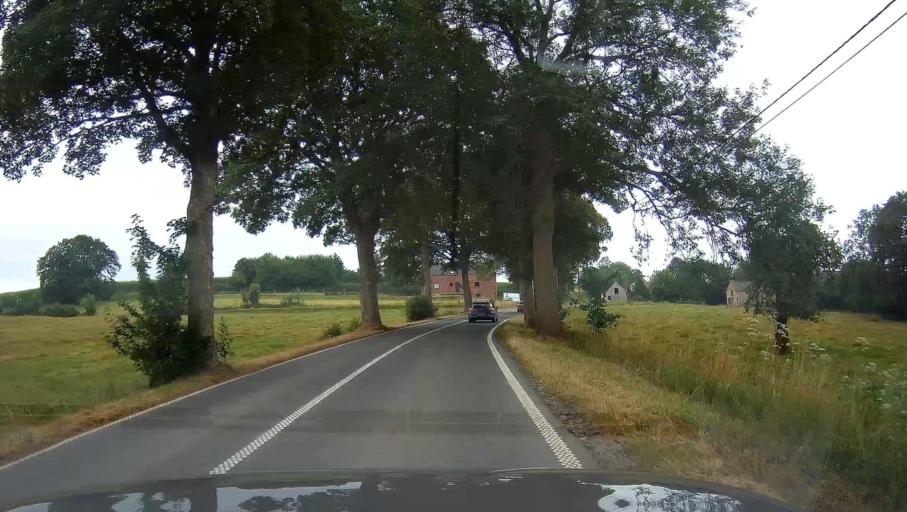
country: BE
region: Wallonia
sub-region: Province de Namur
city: Assesse
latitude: 50.3517
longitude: 5.0468
